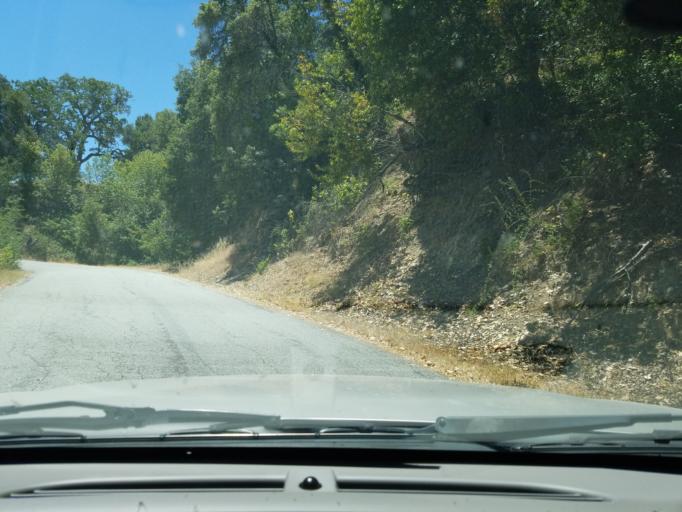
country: US
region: California
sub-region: Monterey County
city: Gonzales
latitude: 36.3402
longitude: -121.5267
